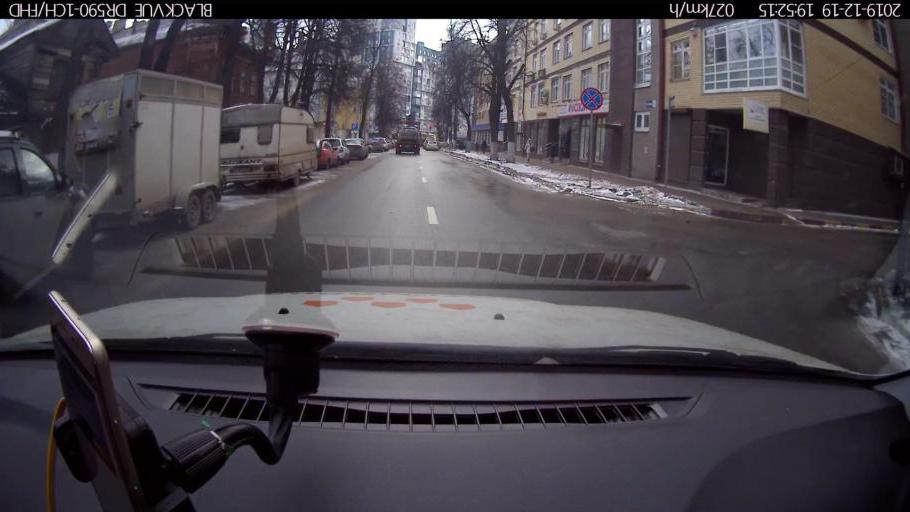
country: RU
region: Nizjnij Novgorod
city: Nizhniy Novgorod
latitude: 56.3112
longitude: 43.9973
